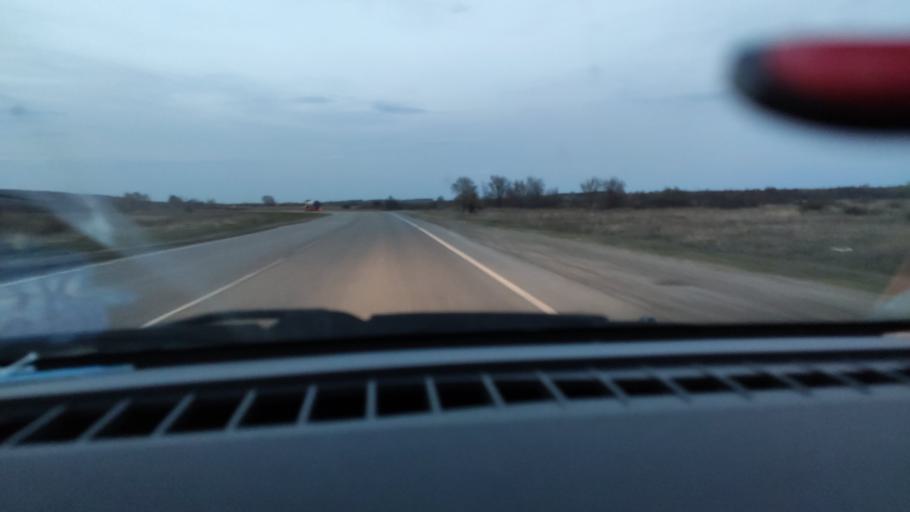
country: RU
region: Saratov
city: Sinodskoye
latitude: 52.0530
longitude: 46.7553
